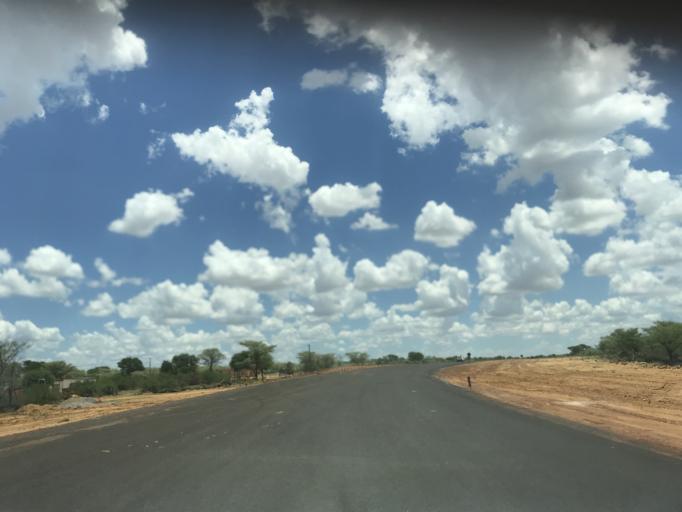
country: BW
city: Mabuli
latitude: -25.8050
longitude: 24.7046
